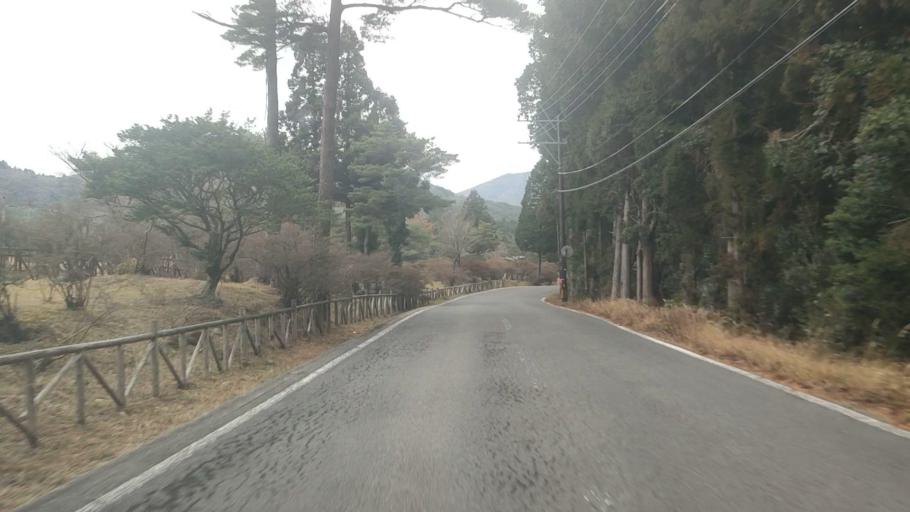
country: JP
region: Nagasaki
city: Shimabara
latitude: 32.7466
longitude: 130.2720
